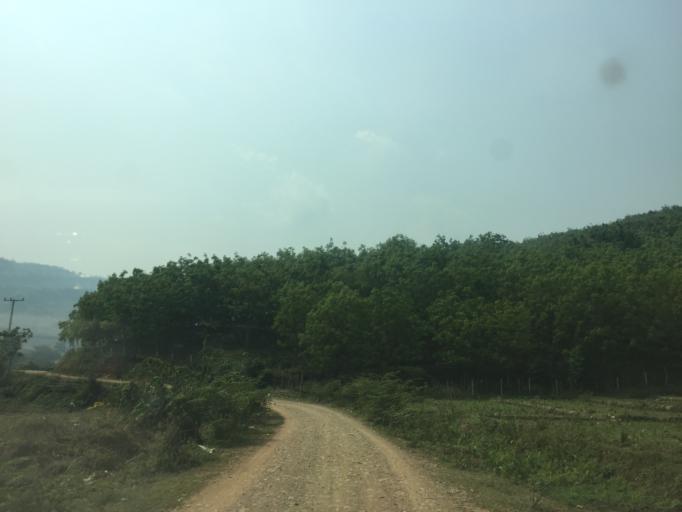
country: TH
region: Phayao
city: Phu Sang
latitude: 19.5727
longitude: 100.5253
